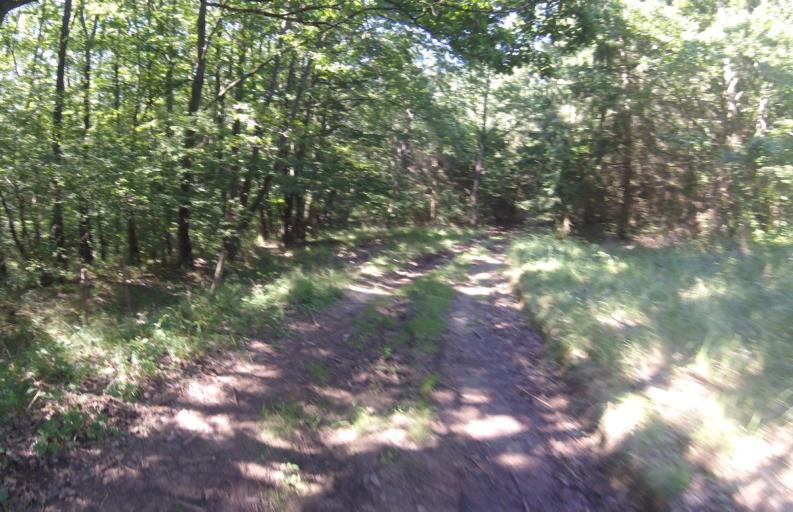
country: HU
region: Pest
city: Szob
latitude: 47.8958
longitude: 18.8765
